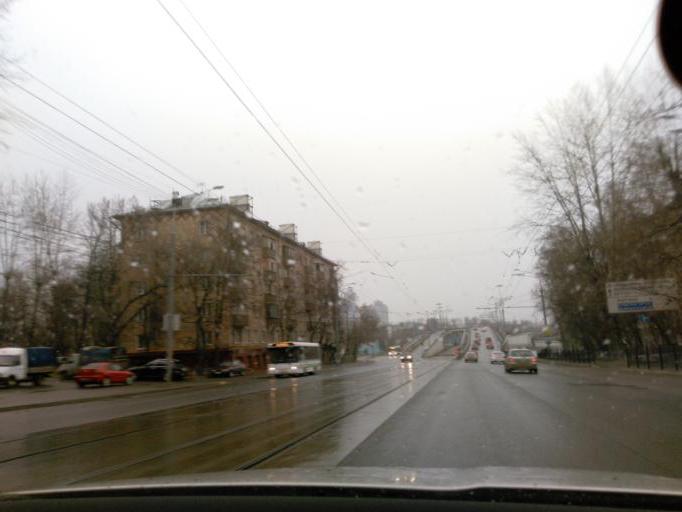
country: RU
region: Moscow
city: Pokrovskoye-Streshnevo
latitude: 55.8240
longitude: 37.4513
